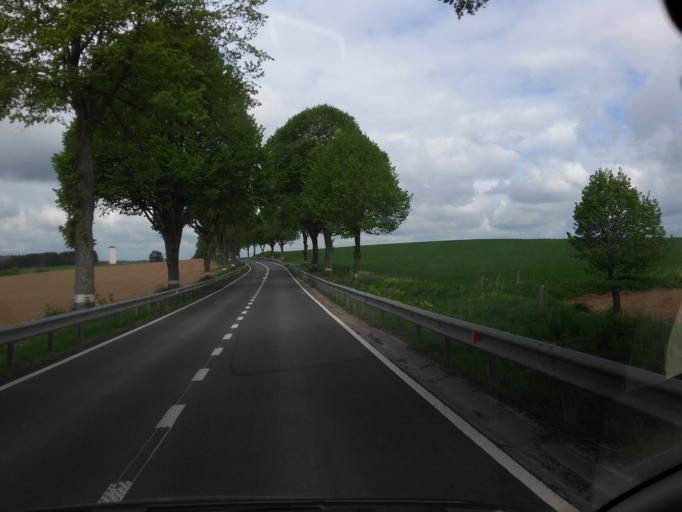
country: BE
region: Wallonia
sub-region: Province du Luxembourg
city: Neufchateau
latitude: 49.8432
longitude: 5.3947
